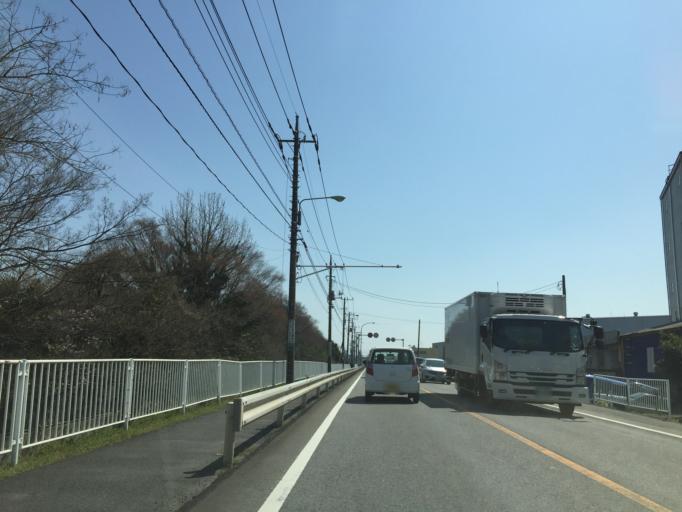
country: JP
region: Saitama
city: Shiki
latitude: 35.8597
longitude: 139.6055
